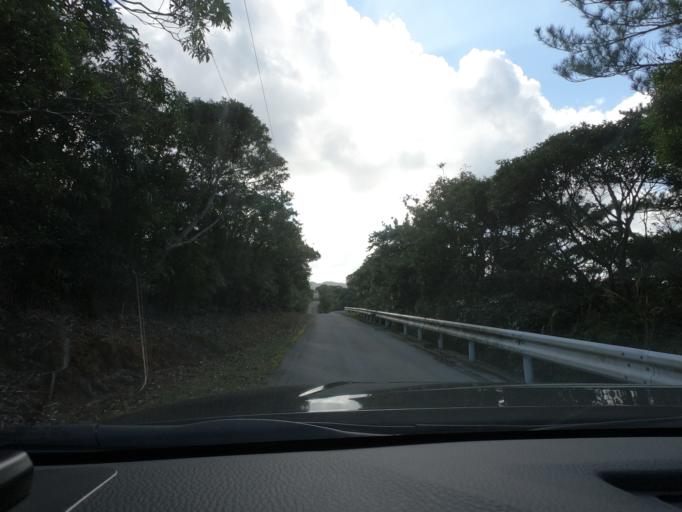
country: JP
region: Okinawa
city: Nago
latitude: 26.7545
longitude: 128.2084
